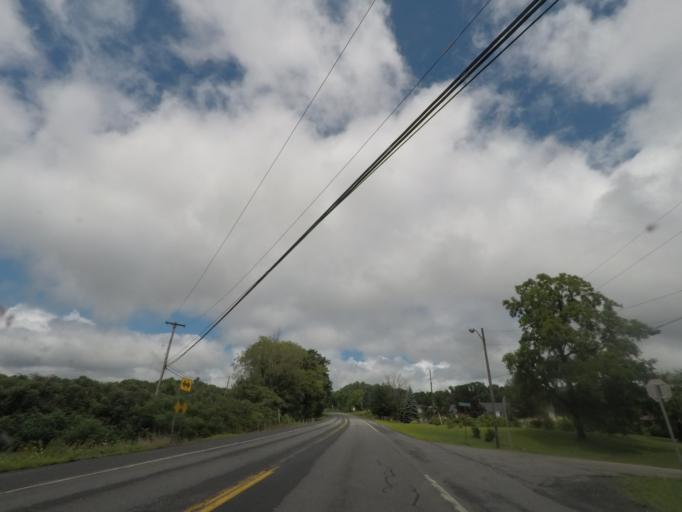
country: US
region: Massachusetts
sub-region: Berkshire County
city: Lanesborough
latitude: 42.5969
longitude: -73.3692
